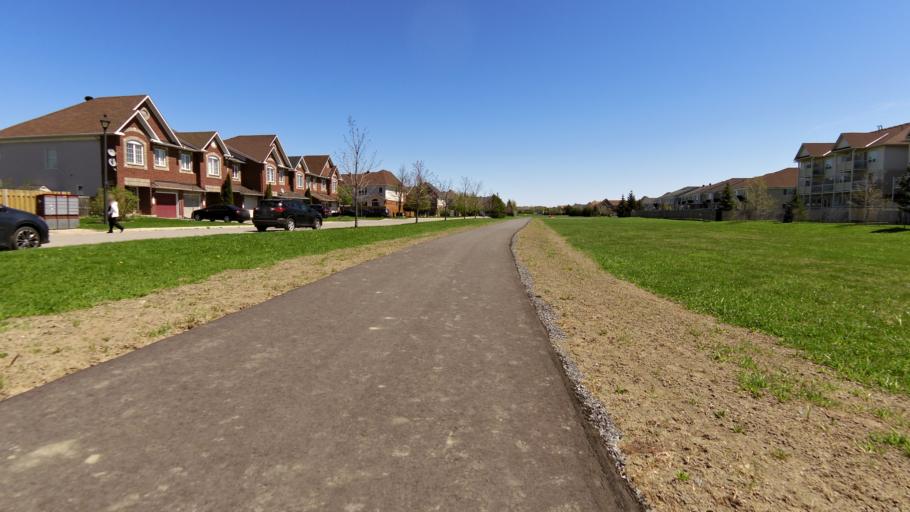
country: CA
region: Ontario
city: Clarence-Rockland
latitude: 45.4589
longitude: -75.4813
